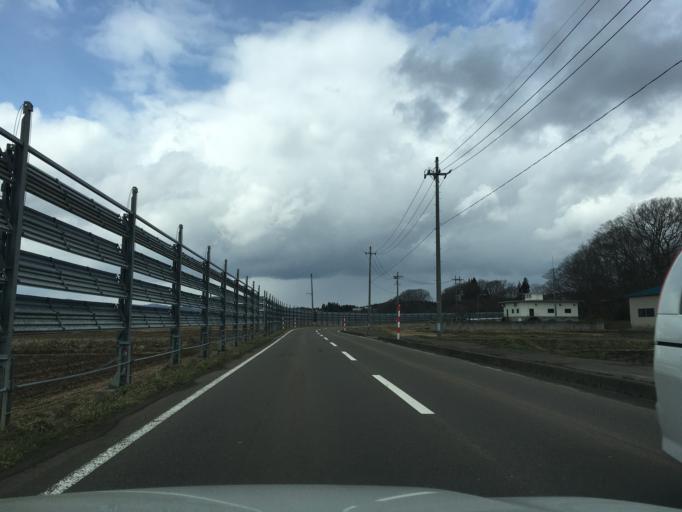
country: JP
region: Akita
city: Takanosu
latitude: 40.1518
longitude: 140.3365
